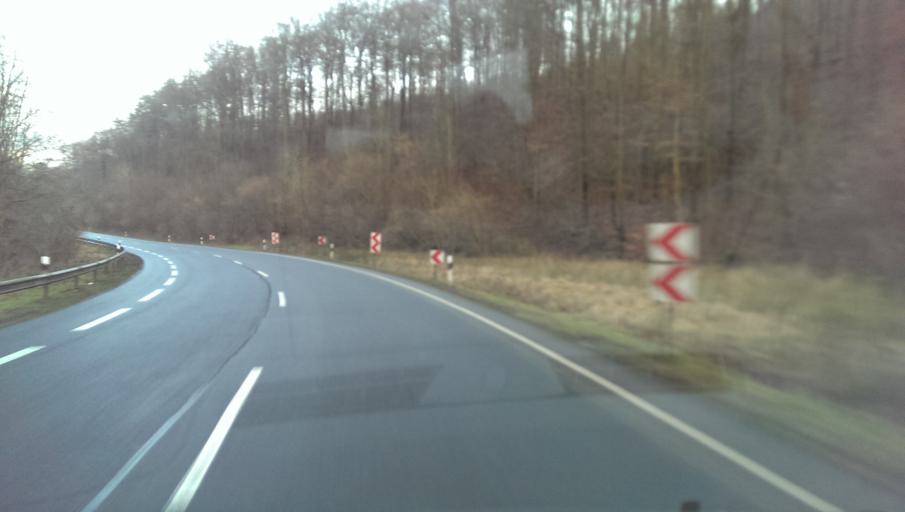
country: DE
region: Lower Saxony
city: Kreiensen
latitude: 51.8590
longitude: 9.9247
